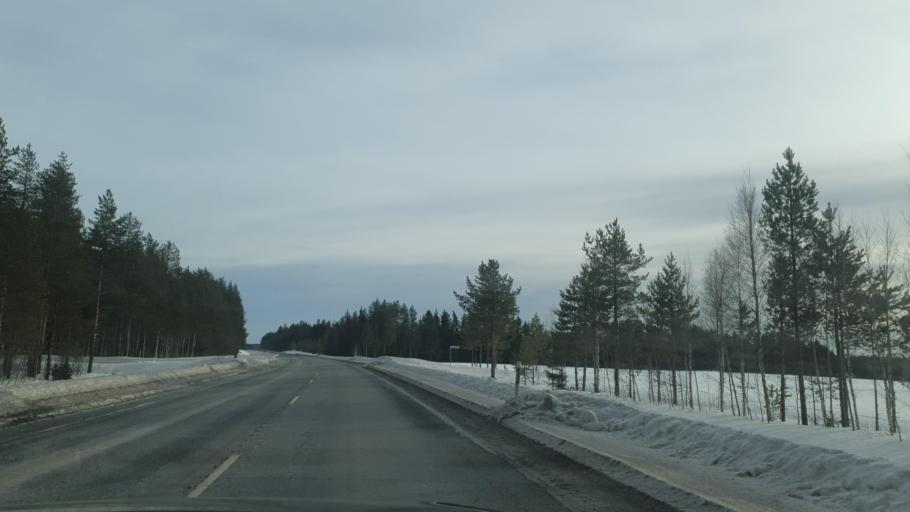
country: FI
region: Kainuu
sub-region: Kajaani
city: Vaala
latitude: 64.6227
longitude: 26.5960
